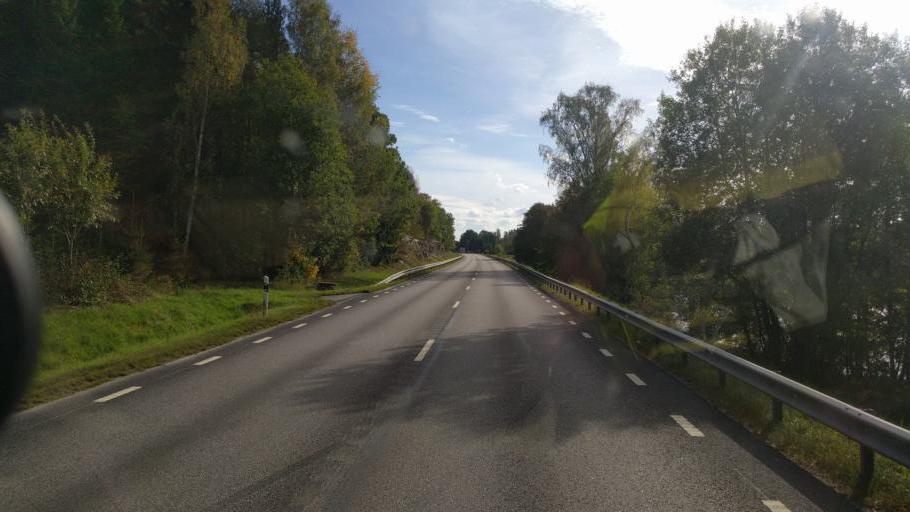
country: SE
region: OEstergoetland
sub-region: Kinda Kommun
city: Kisa
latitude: 57.9330
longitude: 15.6695
